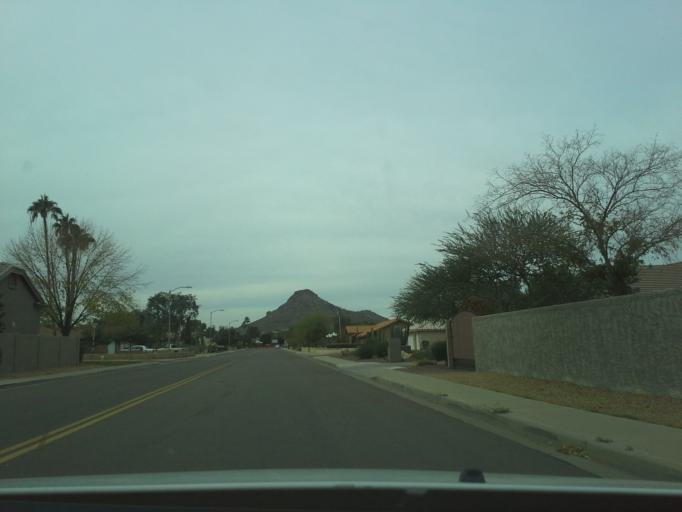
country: US
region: Arizona
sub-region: Maricopa County
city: Paradise Valley
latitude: 33.6226
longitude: -112.0235
